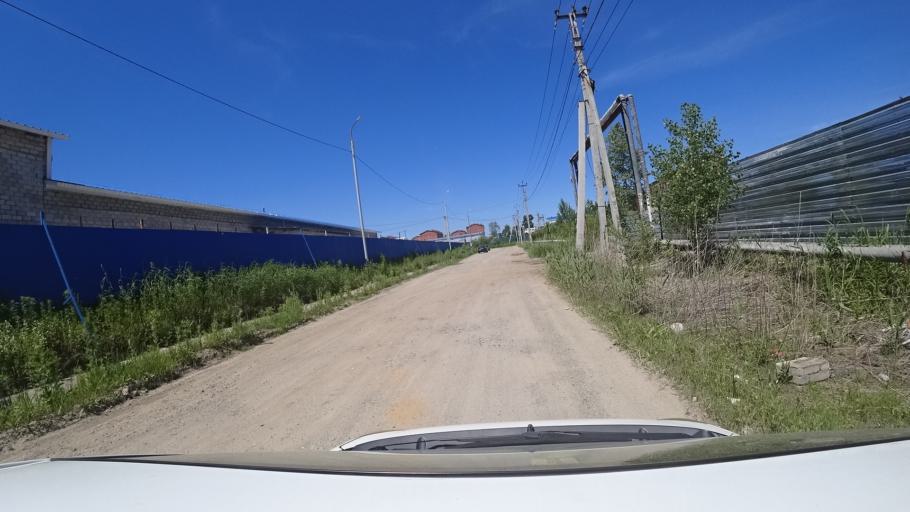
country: RU
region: Khabarovsk Krai
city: Topolevo
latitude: 48.5039
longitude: 135.1815
